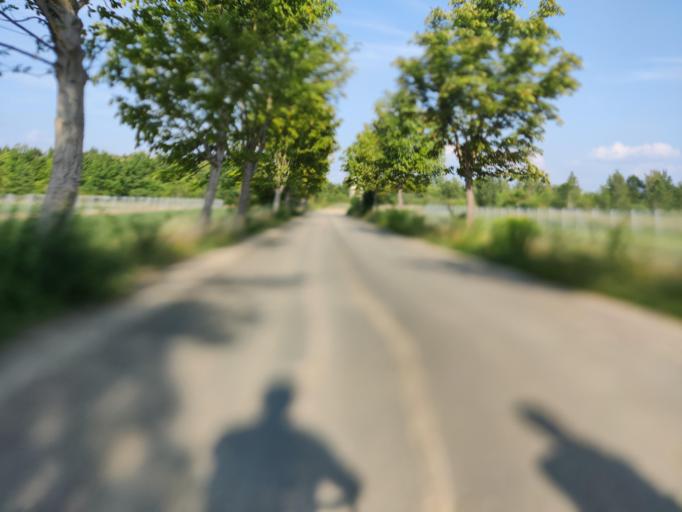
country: DE
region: Saxony
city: Neukieritzsch
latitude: 51.1599
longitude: 12.4293
